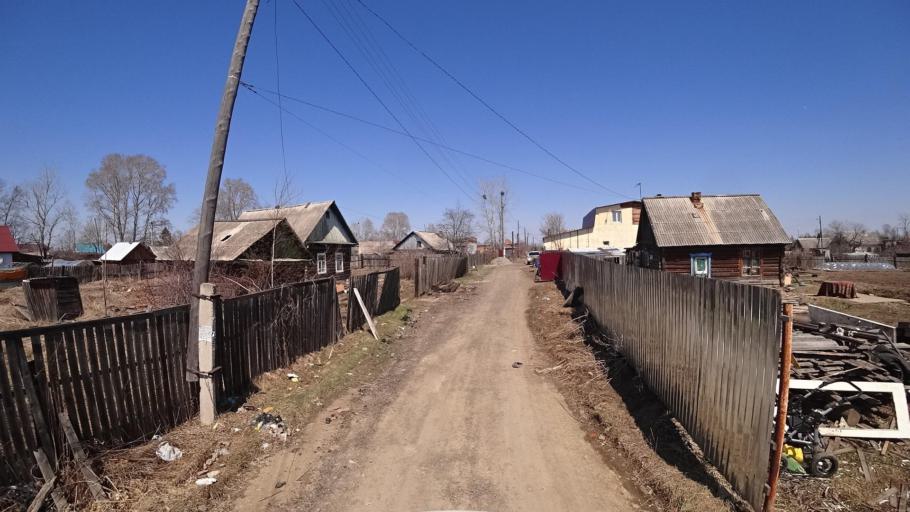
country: RU
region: Khabarovsk Krai
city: Khurba
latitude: 50.4054
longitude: 136.8820
